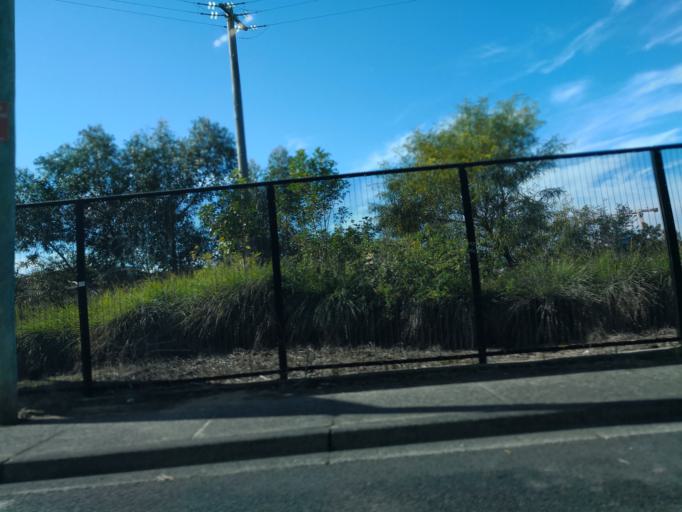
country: AU
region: New South Wales
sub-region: Gosford Shire
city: Gosford
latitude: -33.4260
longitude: 151.3391
